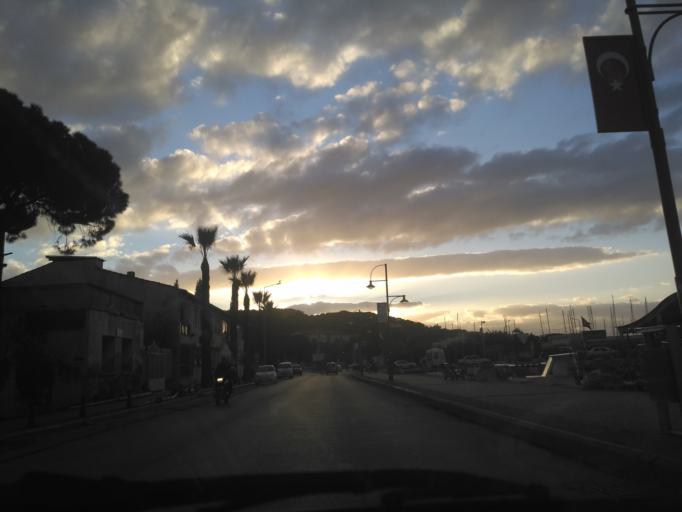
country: TR
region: Balikesir
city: Ayvalik
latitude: 39.3132
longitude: 26.6895
